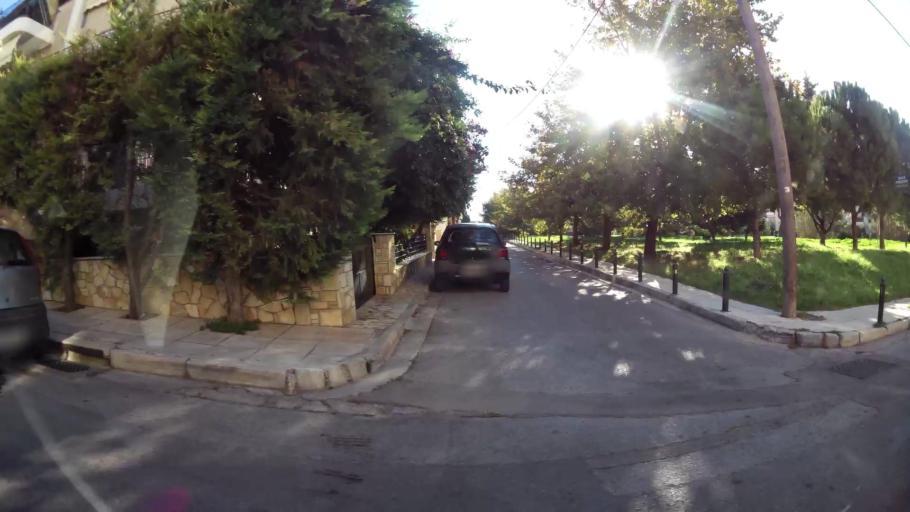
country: GR
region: Attica
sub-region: Nomarchia Anatolikis Attikis
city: Gerakas
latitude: 38.0104
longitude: 23.8612
